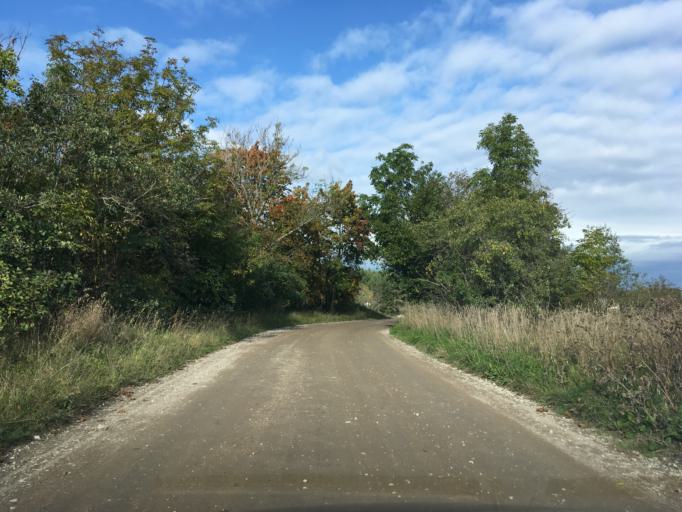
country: EE
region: Harju
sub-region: Saue vald
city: Laagri
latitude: 59.3400
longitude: 24.6498
